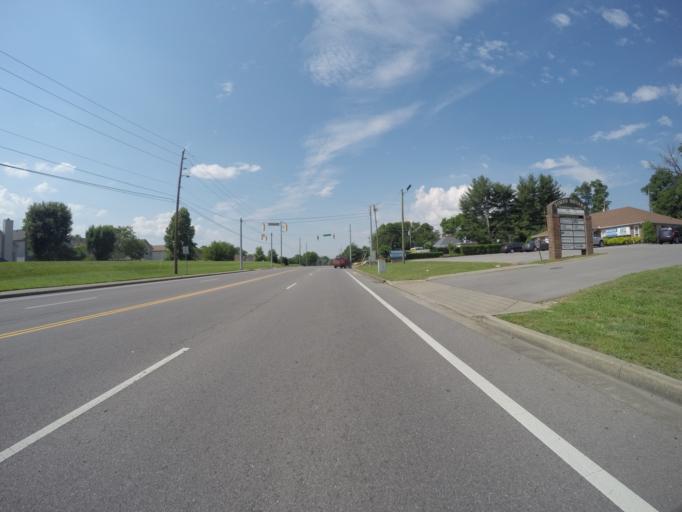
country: US
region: Tennessee
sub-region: Davidson County
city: Lakewood
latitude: 36.2191
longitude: -86.5976
